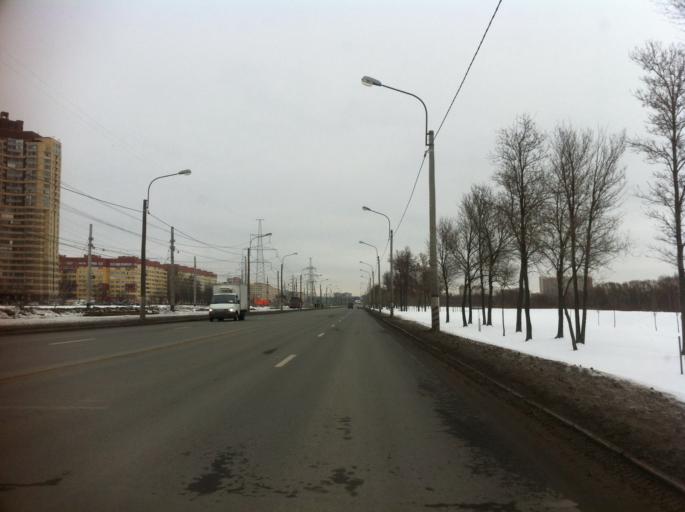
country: RU
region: St.-Petersburg
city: Uritsk
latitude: 59.8461
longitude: 30.1824
